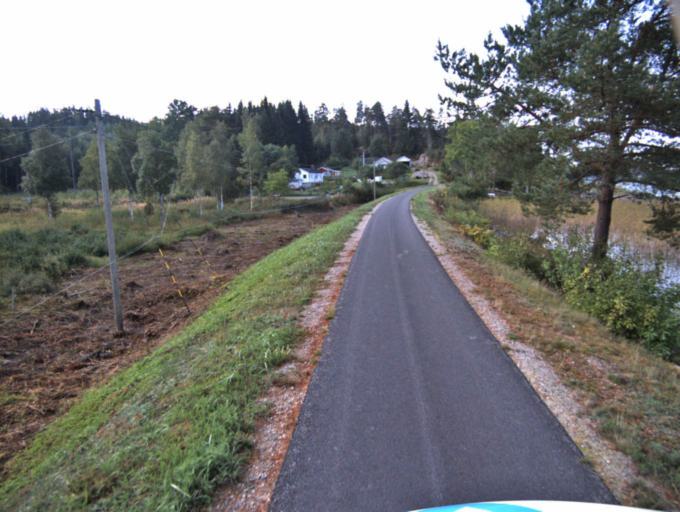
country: SE
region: Vaestra Goetaland
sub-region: Ulricehamns Kommun
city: Ulricehamn
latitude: 57.7070
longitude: 13.3980
